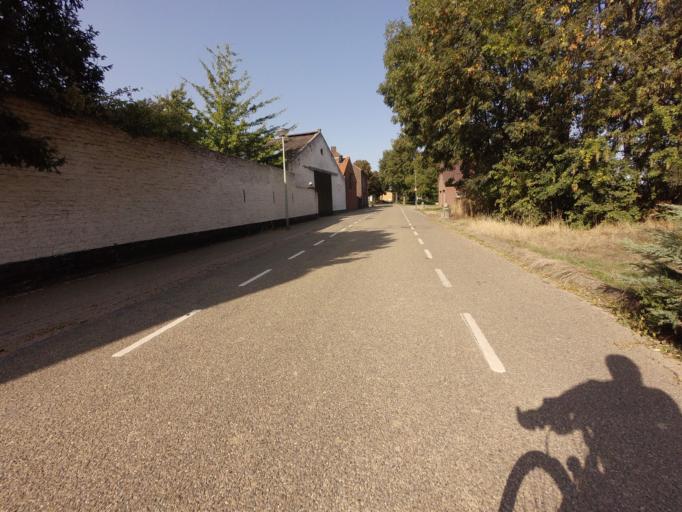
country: NL
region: Limburg
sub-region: Gemeente Maasgouw
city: Maasbracht
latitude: 51.1285
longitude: 5.8546
